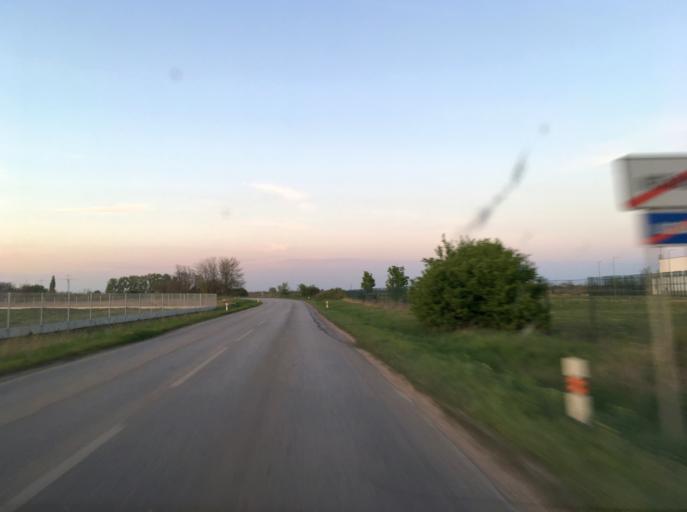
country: SK
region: Nitriansky
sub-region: Okres Nove Zamky
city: Nove Zamky
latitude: 47.9371
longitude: 18.1269
